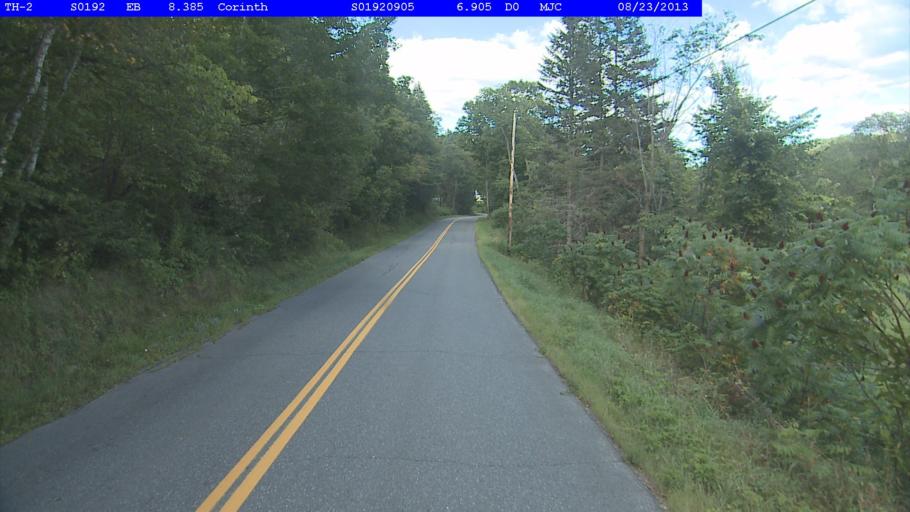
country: US
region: New Hampshire
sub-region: Grafton County
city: Orford
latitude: 44.0097
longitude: -72.2400
